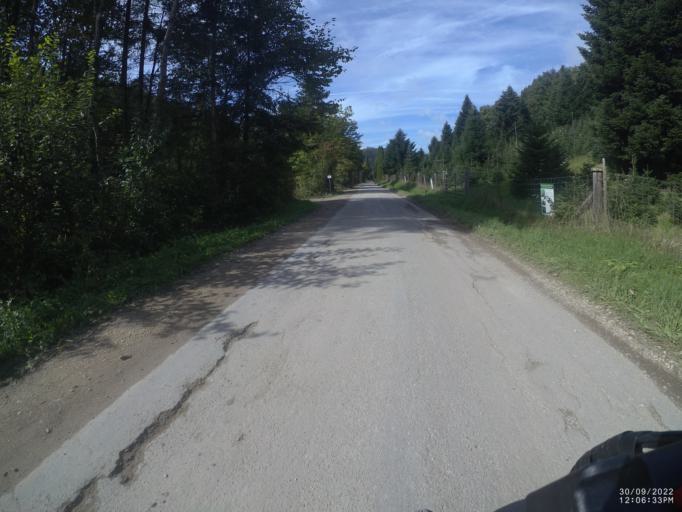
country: DE
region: Baden-Wuerttemberg
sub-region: Regierungsbezirk Stuttgart
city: Wangen
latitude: 48.7476
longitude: 9.6113
